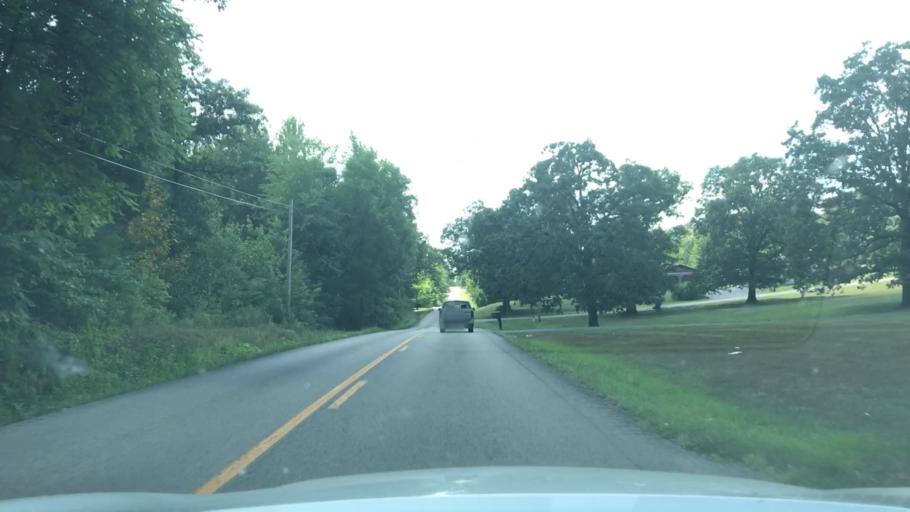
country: US
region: Kentucky
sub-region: Muhlenberg County
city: Greenville
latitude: 37.1863
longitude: -87.2248
